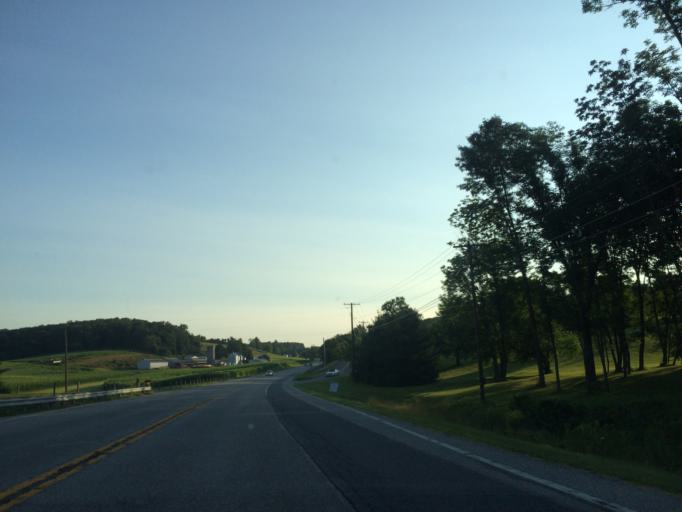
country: US
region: Maryland
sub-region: Carroll County
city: Westminster
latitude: 39.6118
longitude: -76.9416
